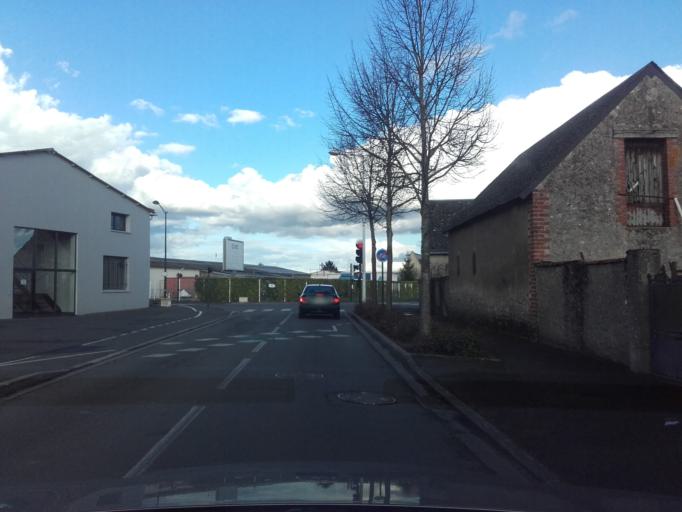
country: FR
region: Centre
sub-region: Departement d'Indre-et-Loire
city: Mettray
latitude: 47.4297
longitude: 0.6671
